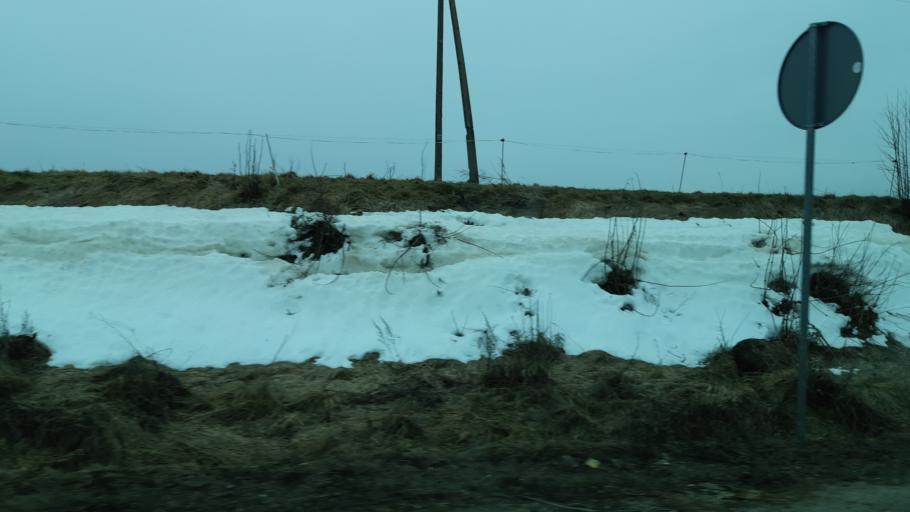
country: PL
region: Podlasie
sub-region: Suwalki
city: Suwalki
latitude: 54.3338
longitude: 22.9343
